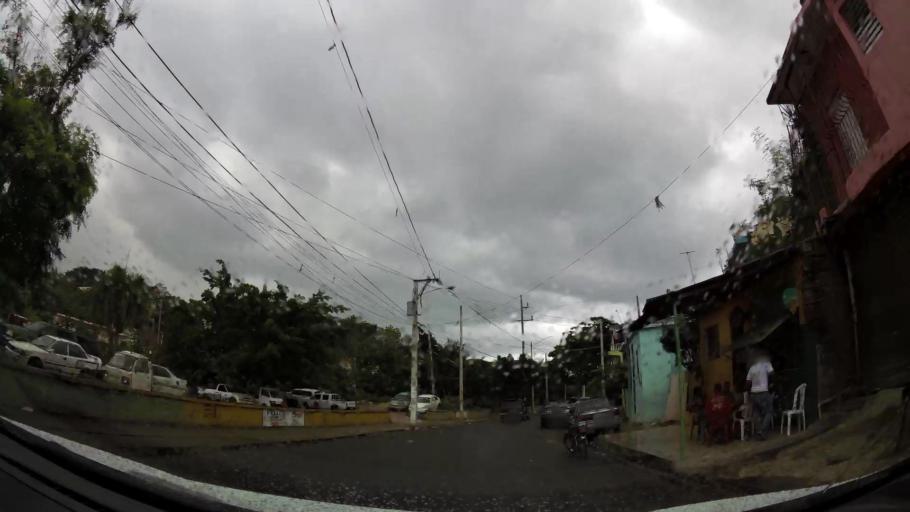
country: DO
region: Nacional
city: La Agustina
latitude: 18.5003
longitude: -69.9320
